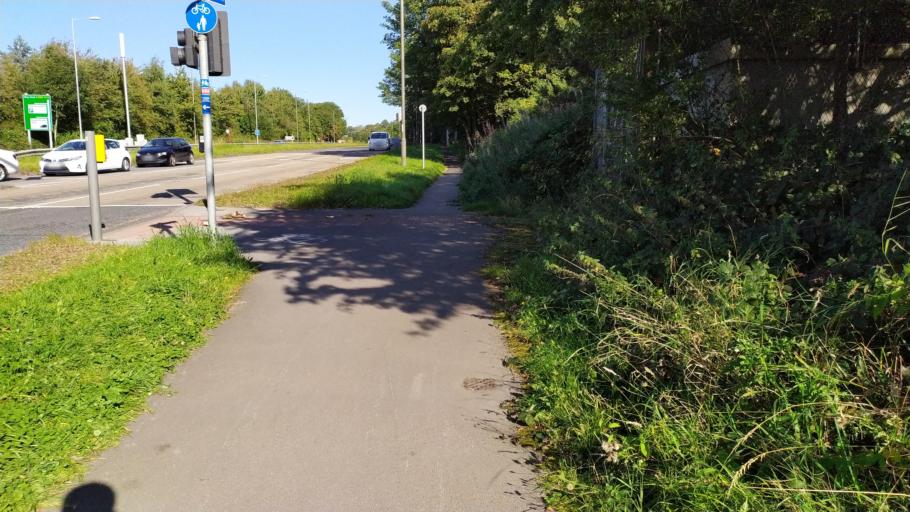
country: GB
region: England
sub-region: City and Borough of Leeds
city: Chapel Allerton
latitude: 53.8426
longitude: -1.5572
